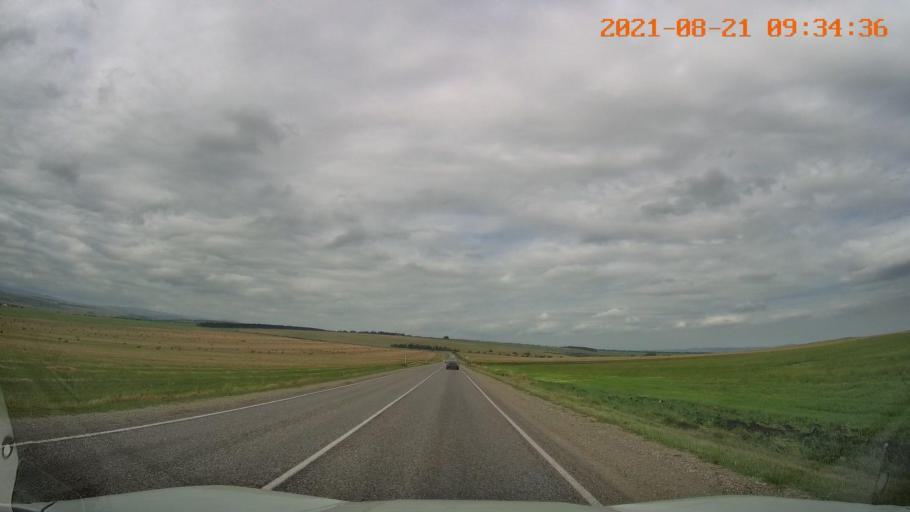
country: RU
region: Stavropol'skiy
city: Yutsa
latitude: 43.9925
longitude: 42.9709
